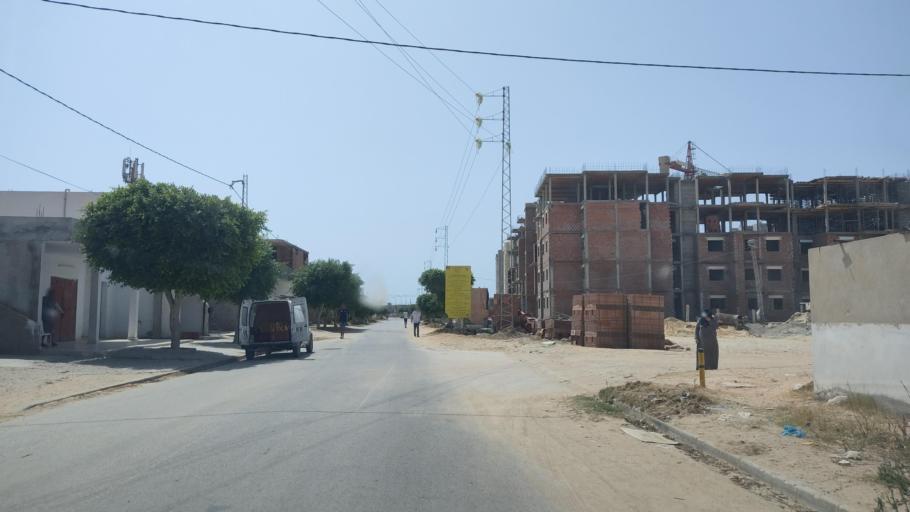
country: TN
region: Safaqis
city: Sfax
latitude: 34.6699
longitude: 10.7057
